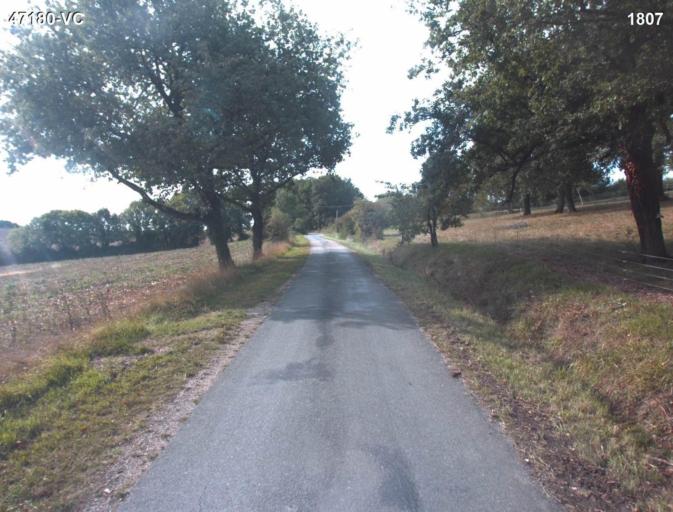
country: FR
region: Aquitaine
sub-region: Departement du Lot-et-Garonne
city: Sainte-Colombe-en-Bruilhois
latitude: 44.1744
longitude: 0.4420
